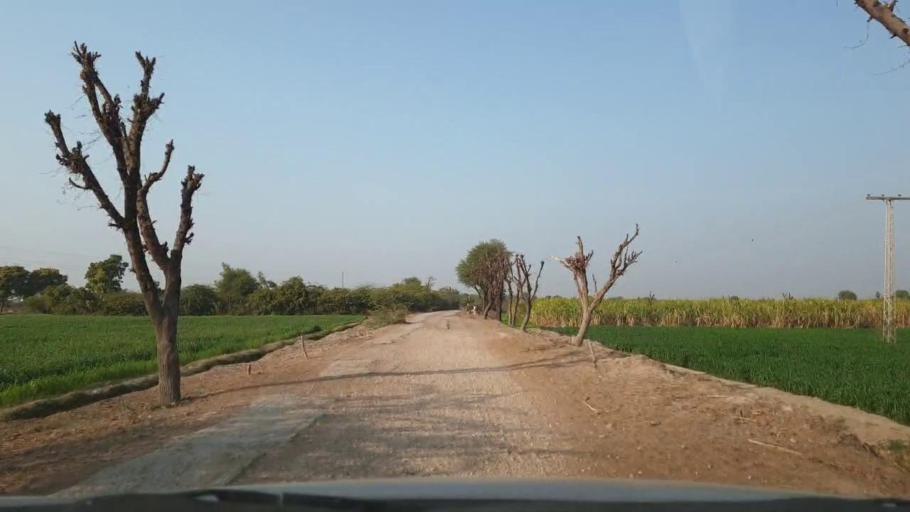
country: PK
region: Sindh
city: Tando Adam
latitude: 25.6848
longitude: 68.6329
